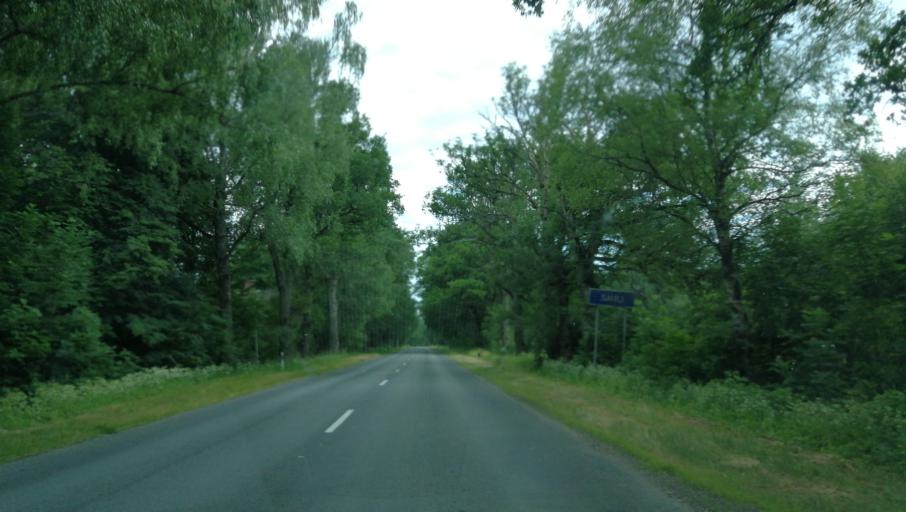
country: LV
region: Valmieras Rajons
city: Valmiera
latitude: 57.6645
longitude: 25.4291
